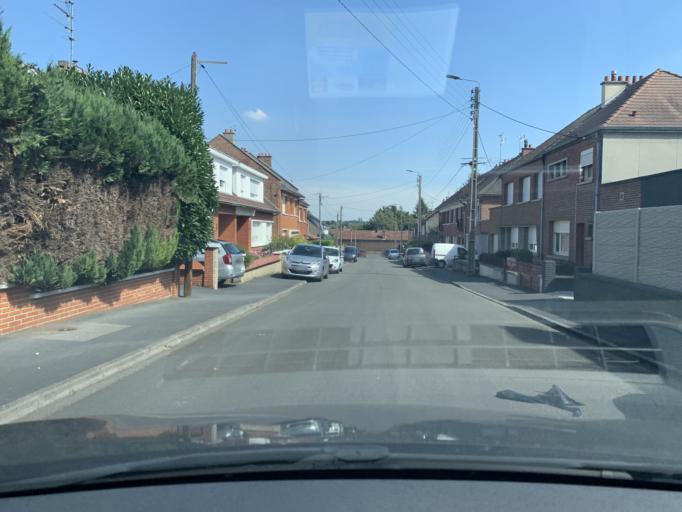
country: FR
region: Nord-Pas-de-Calais
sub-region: Departement du Nord
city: Cambrai
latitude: 50.1655
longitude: 3.2334
